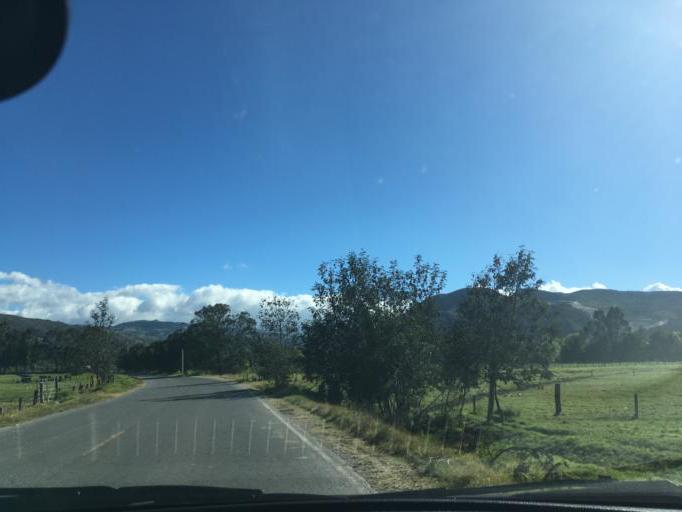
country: CO
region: Boyaca
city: Firavitoba
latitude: 5.6294
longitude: -72.9844
